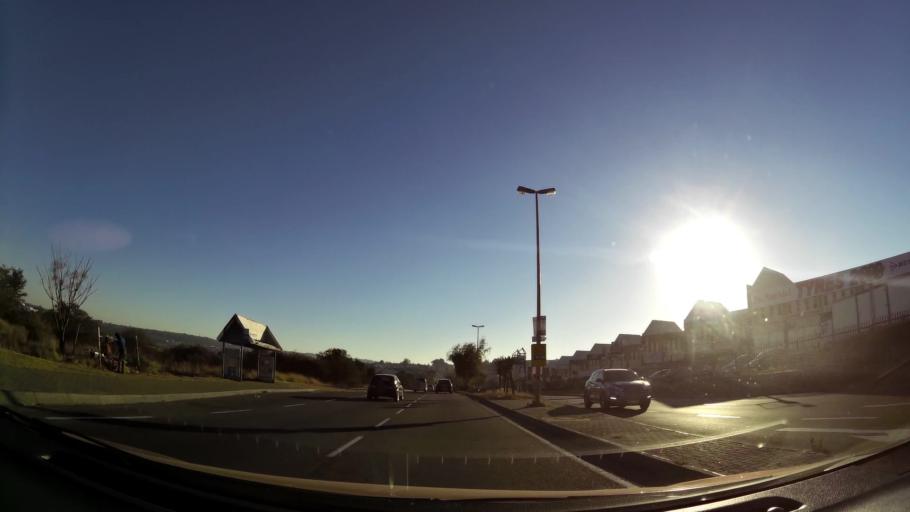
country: ZA
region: Gauteng
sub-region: City of Johannesburg Metropolitan Municipality
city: Midrand
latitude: -26.0086
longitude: 28.1216
